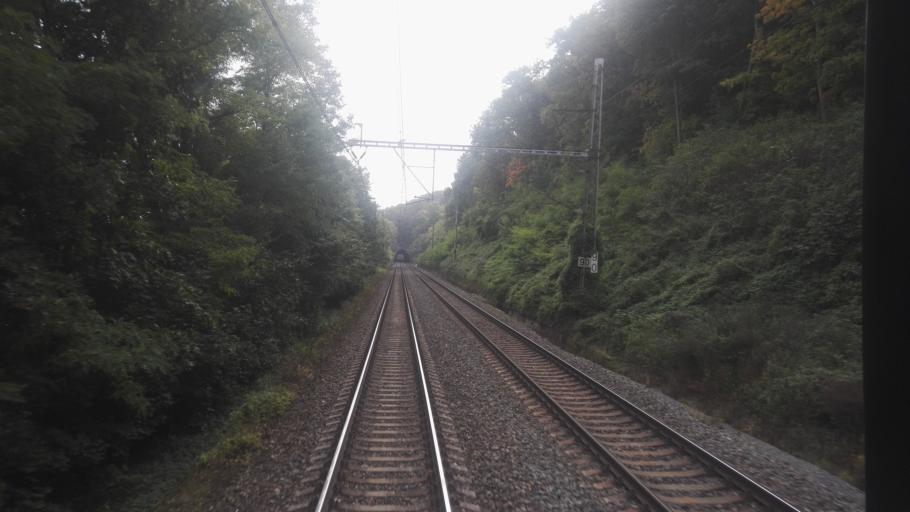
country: CZ
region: Central Bohemia
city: Nelahozeves
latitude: 50.2568
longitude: 14.3014
